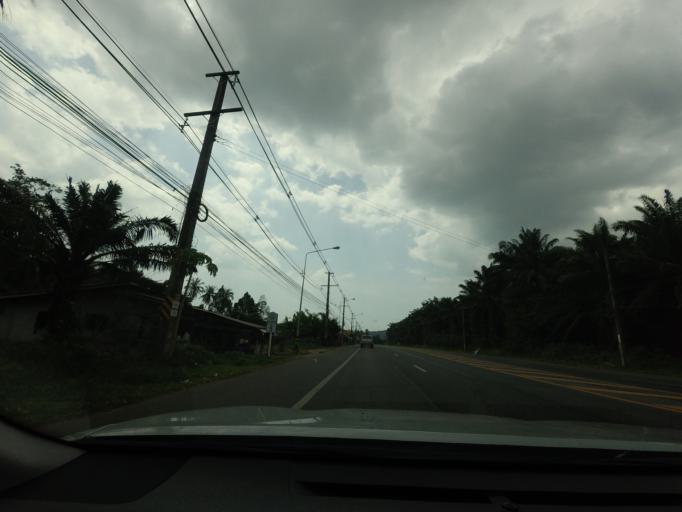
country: TH
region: Phangnga
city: Ban Ao Nang
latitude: 8.0605
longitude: 98.7837
